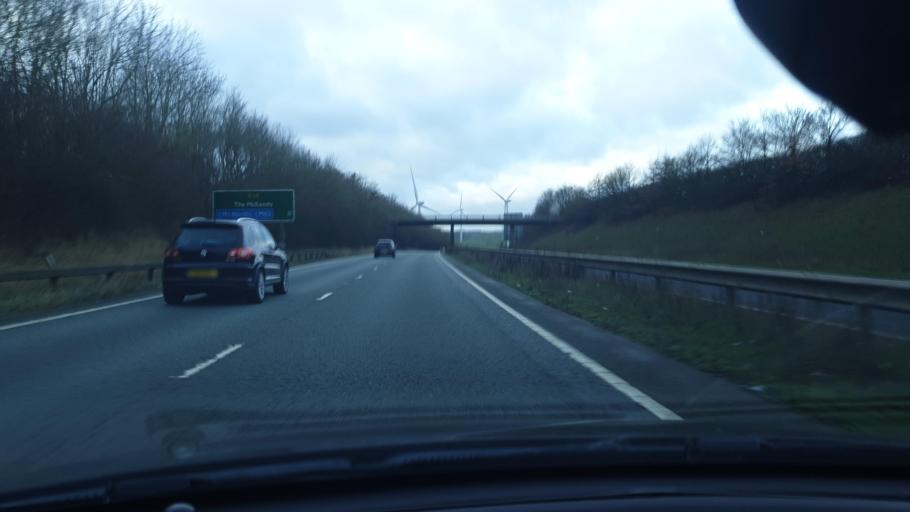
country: GB
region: England
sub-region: Northamptonshire
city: Brixworth
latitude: 52.3998
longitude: -0.9234
